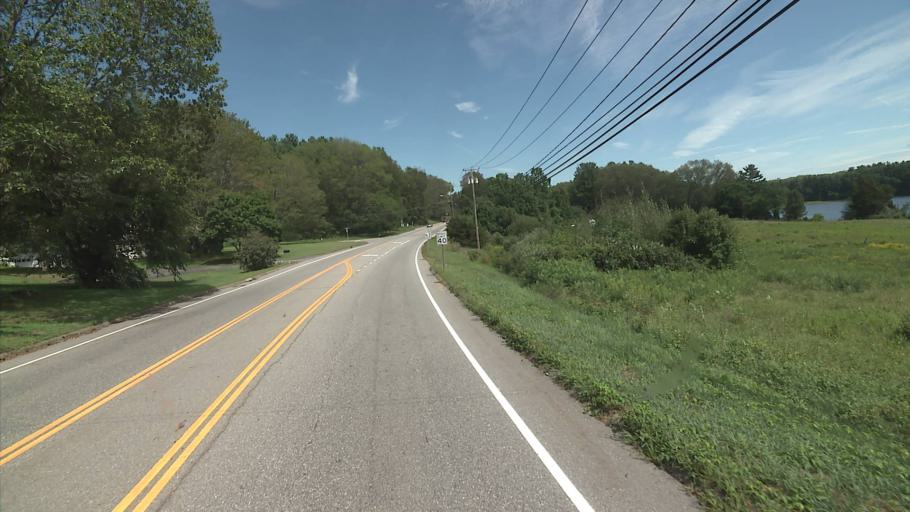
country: US
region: Connecticut
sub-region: Windham County
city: Willimantic
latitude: 41.7442
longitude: -72.1963
